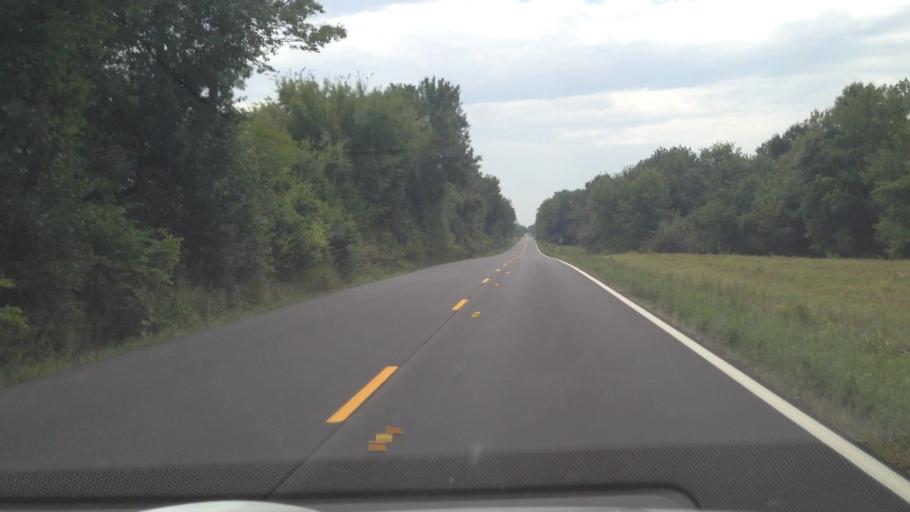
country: US
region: Kansas
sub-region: Crawford County
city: Girard
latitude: 37.5246
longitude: -94.9606
